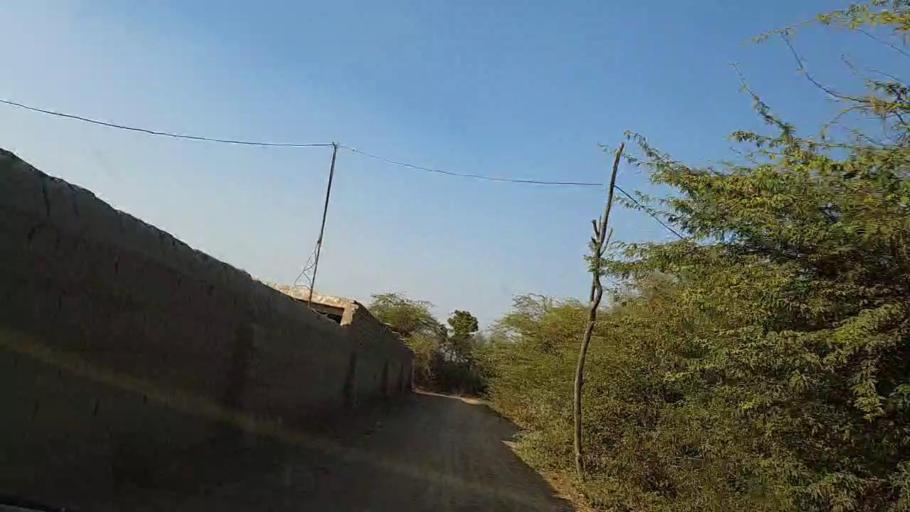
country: PK
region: Sindh
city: Sakrand
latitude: 26.0933
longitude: 68.2068
